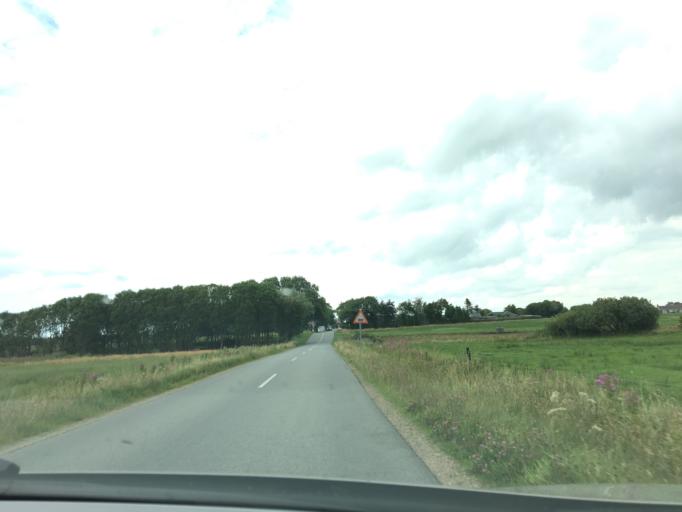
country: DK
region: South Denmark
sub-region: Varde Kommune
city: Oksbol
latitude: 55.7142
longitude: 8.3387
